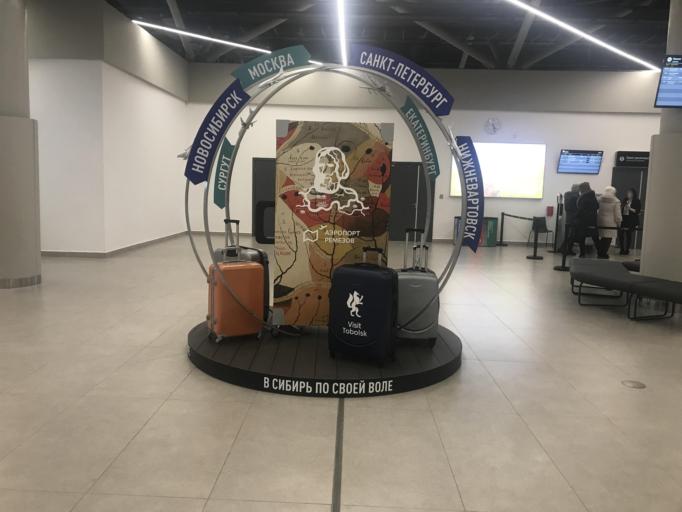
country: RU
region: Tjumen
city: Sumkino
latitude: 58.0617
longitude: 68.3302
